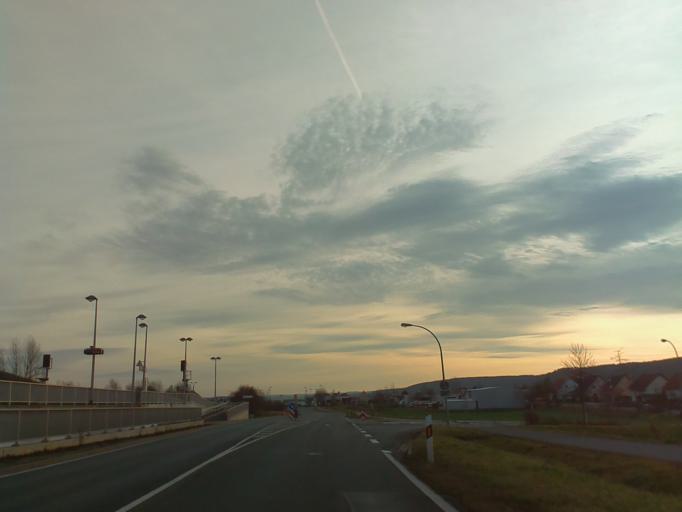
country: DE
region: Thuringia
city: Zollnitz
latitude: 50.8751
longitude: 11.6375
